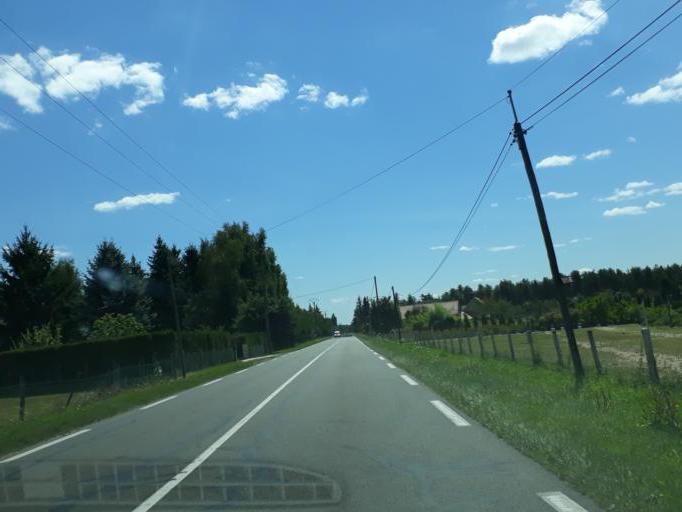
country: FR
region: Centre
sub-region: Departement du Loiret
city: Bray-en-Val
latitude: 47.8111
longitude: 2.3807
